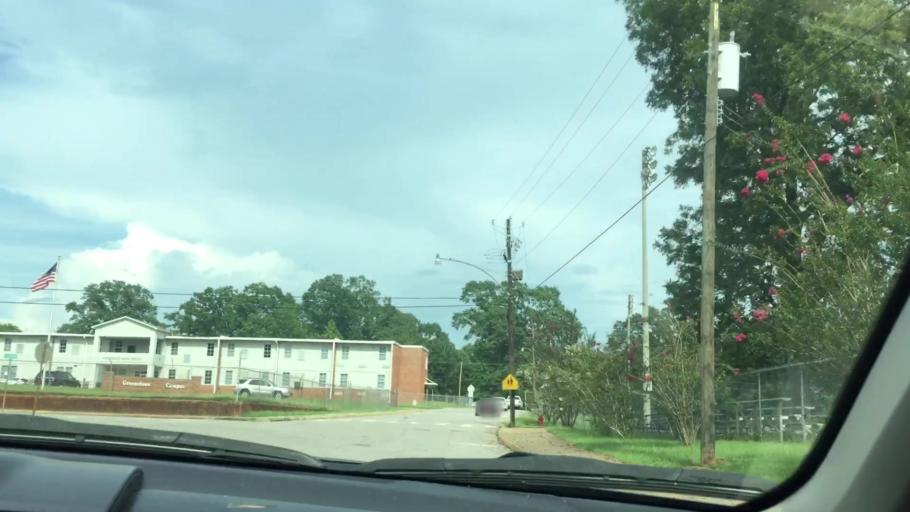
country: US
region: Alabama
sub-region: Hale County
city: Greensboro
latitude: 32.7072
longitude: -87.5891
